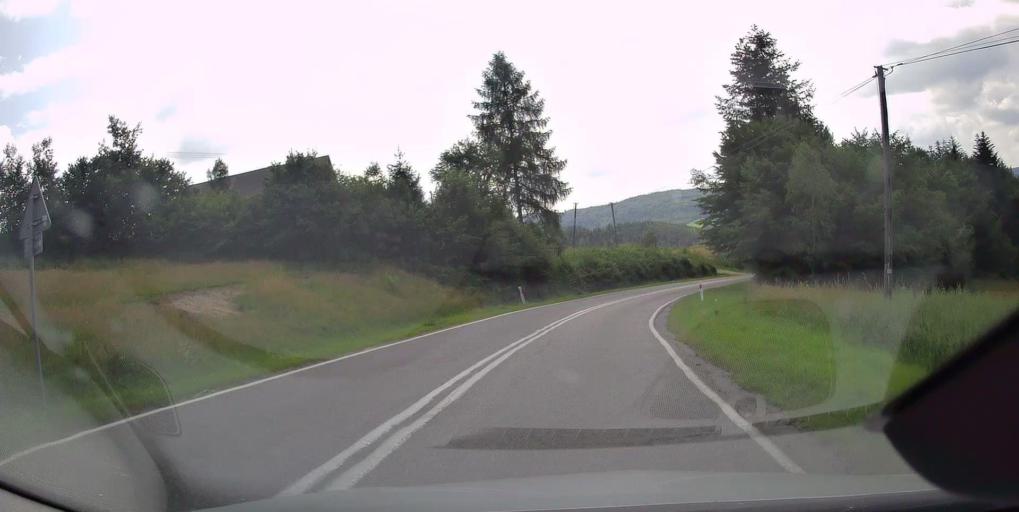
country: PL
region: Lesser Poland Voivodeship
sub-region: Powiat tarnowski
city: Zakliczyn
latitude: 49.7671
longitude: 20.7812
